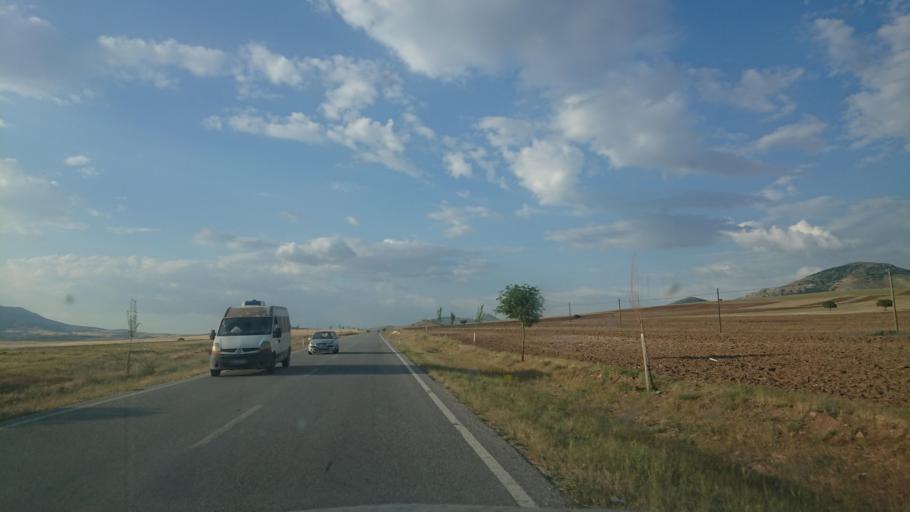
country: TR
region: Aksaray
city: Aksaray
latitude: 38.5312
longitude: 34.0973
